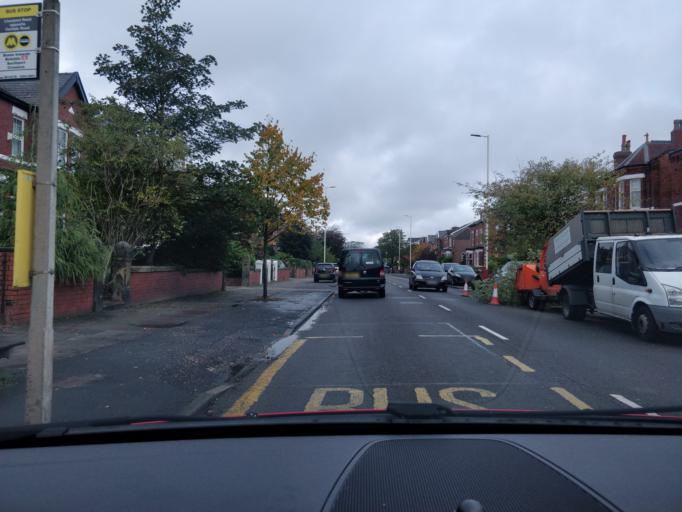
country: GB
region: England
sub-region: Sefton
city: Southport
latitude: 53.6264
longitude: -3.0121
